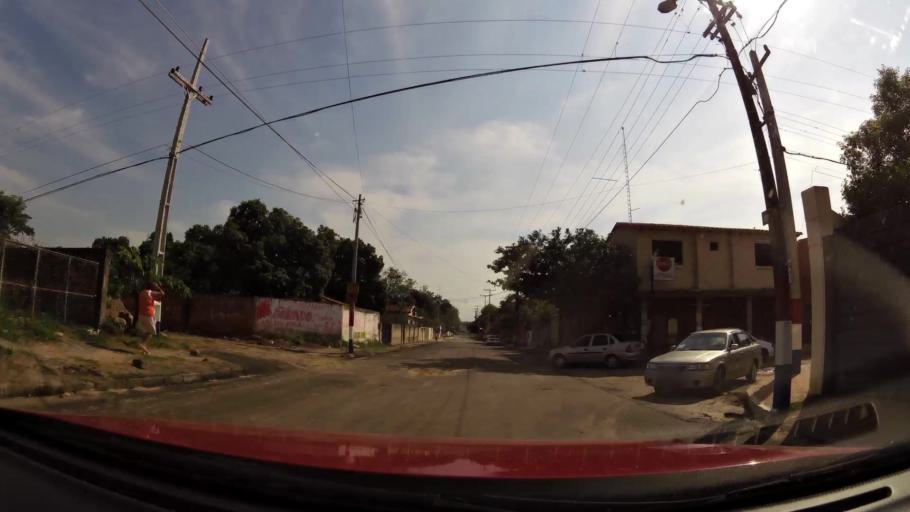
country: PY
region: Central
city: Fernando de la Mora
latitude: -25.2589
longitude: -57.5553
